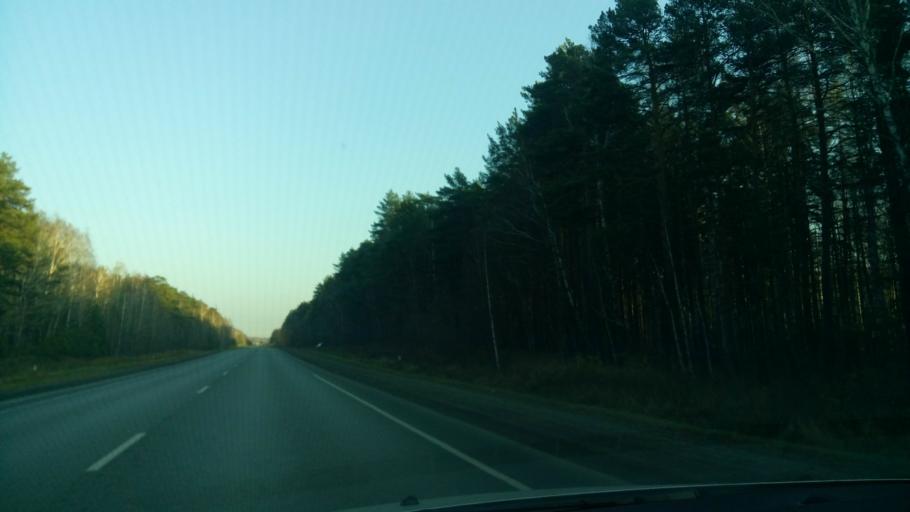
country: RU
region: Sverdlovsk
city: Baraba
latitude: 56.7804
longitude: 61.7876
